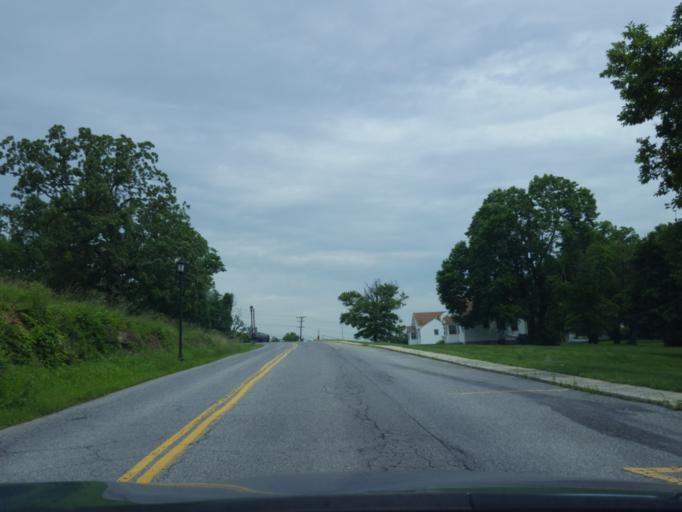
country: US
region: Maryland
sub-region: Carroll County
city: Eldersburg
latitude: 39.3900
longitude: -76.9607
